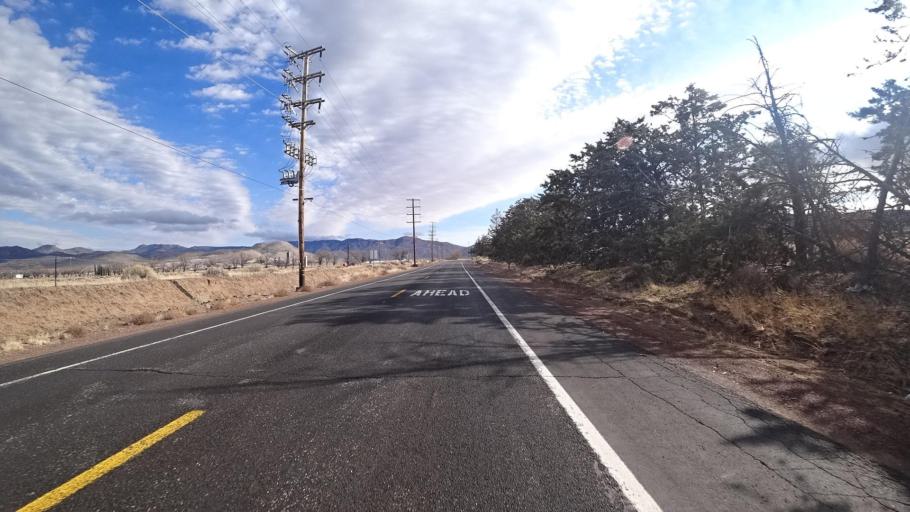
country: US
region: California
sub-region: Kern County
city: Tehachapi
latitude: 35.1097
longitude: -118.3990
